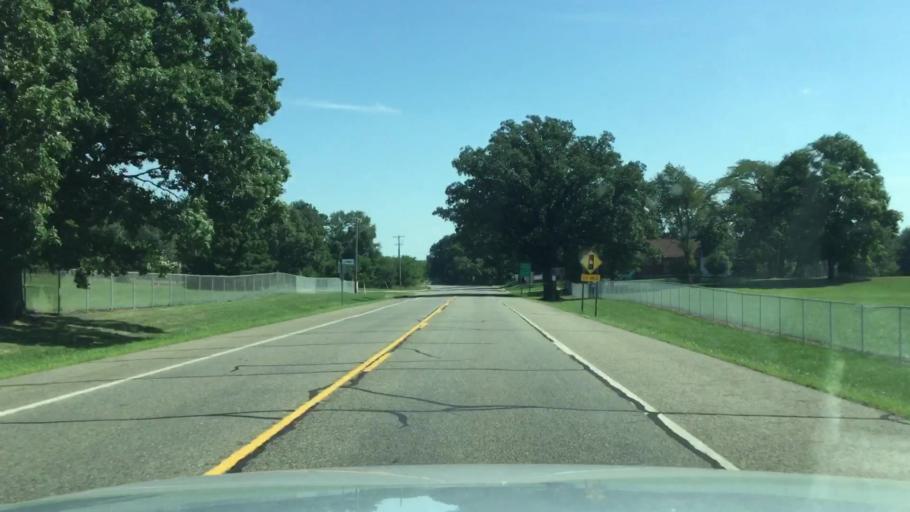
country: US
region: Michigan
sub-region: Jackson County
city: Brooklyn
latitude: 42.0582
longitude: -84.2303
